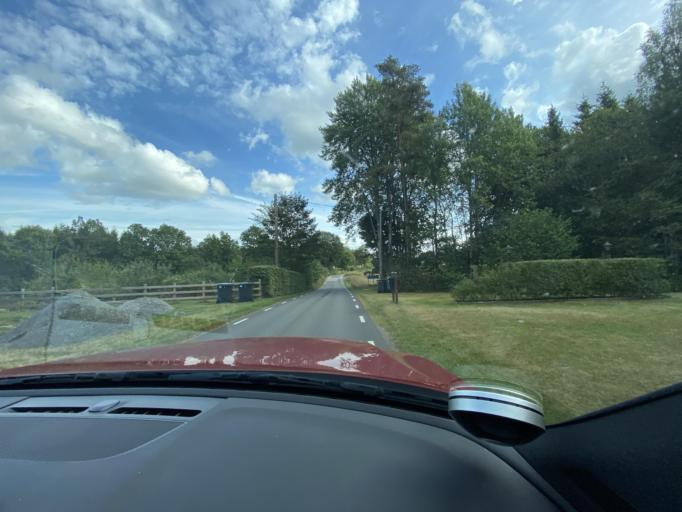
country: SE
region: Skane
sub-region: Hassleholms Kommun
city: Bjarnum
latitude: 56.3570
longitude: 13.8070
